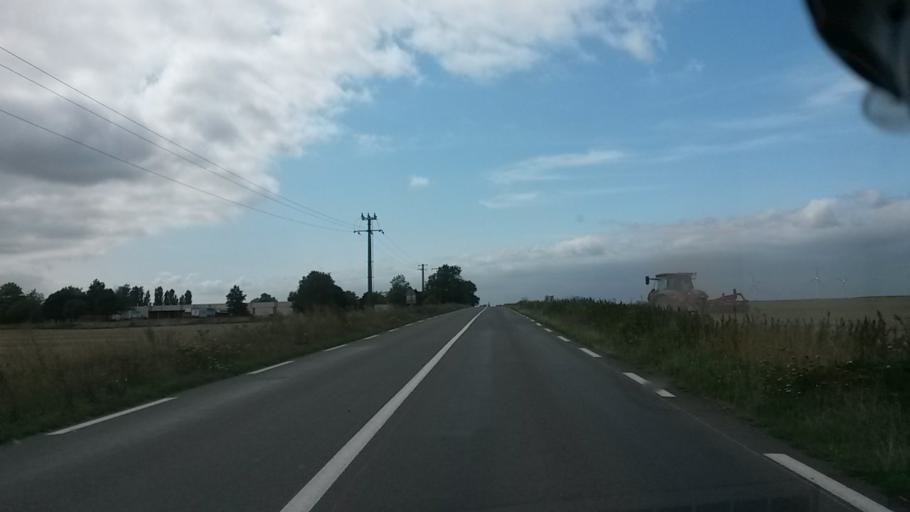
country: FR
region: Nord-Pas-de-Calais
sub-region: Departement du Pas-de-Calais
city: Hermies
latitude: 50.1464
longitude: 3.0633
